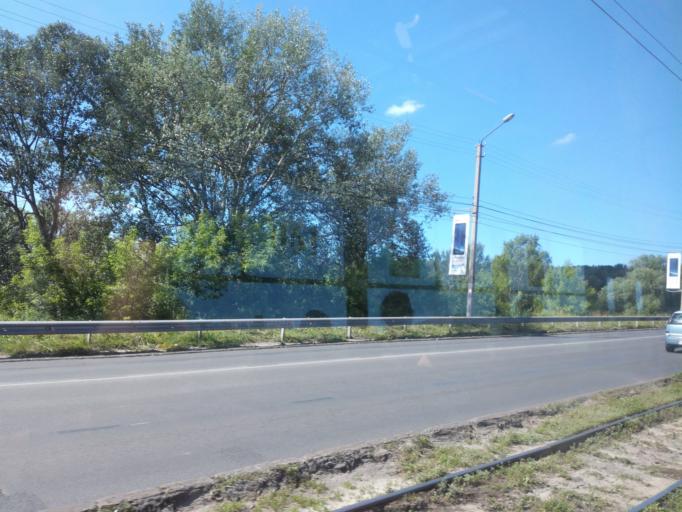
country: RU
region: Kursk
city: Kursk
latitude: 51.7485
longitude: 36.1727
